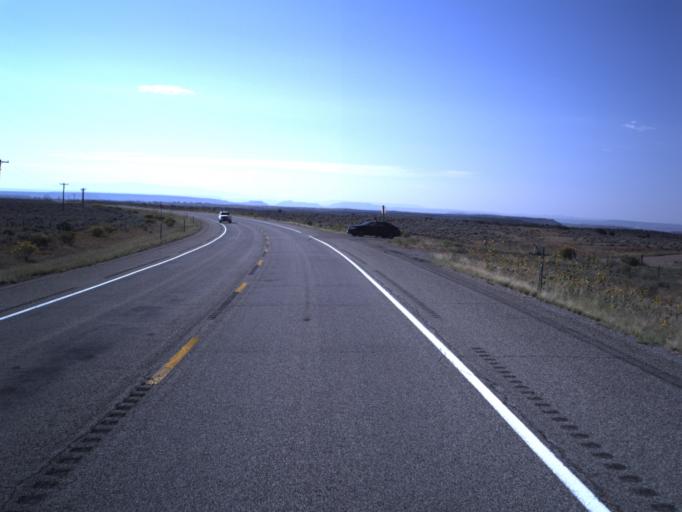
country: US
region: Utah
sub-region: San Juan County
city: Blanding
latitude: 37.5148
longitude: -109.4939
